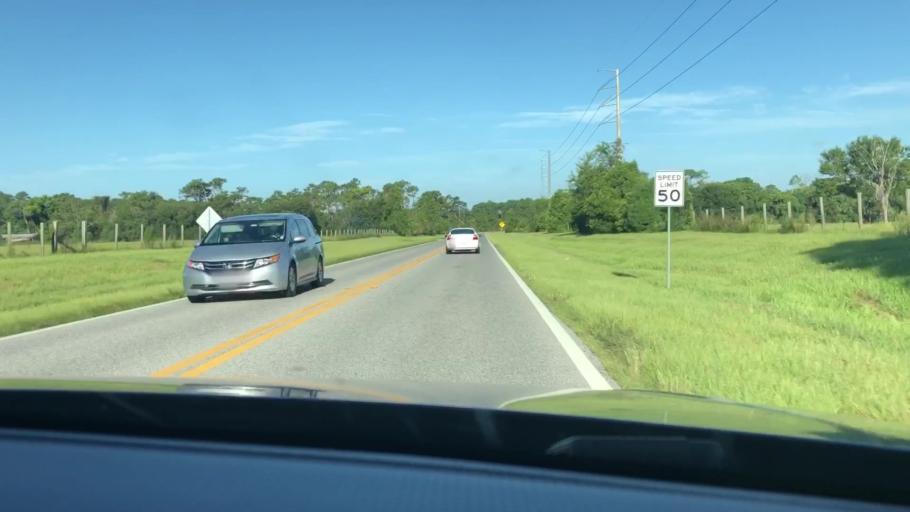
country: US
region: Florida
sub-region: Lake County
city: Eustis
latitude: 28.8693
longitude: -81.6551
